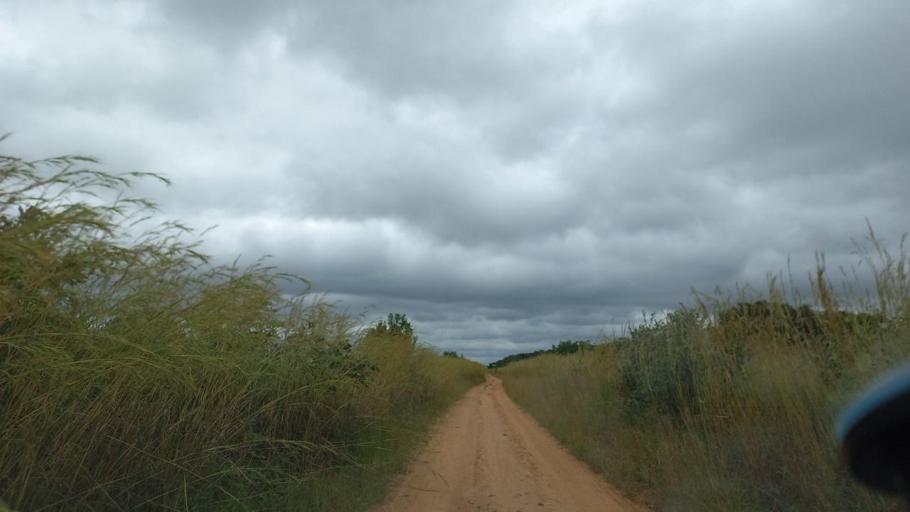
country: ZM
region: Lusaka
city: Lusaka
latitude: -15.1283
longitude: 28.3701
